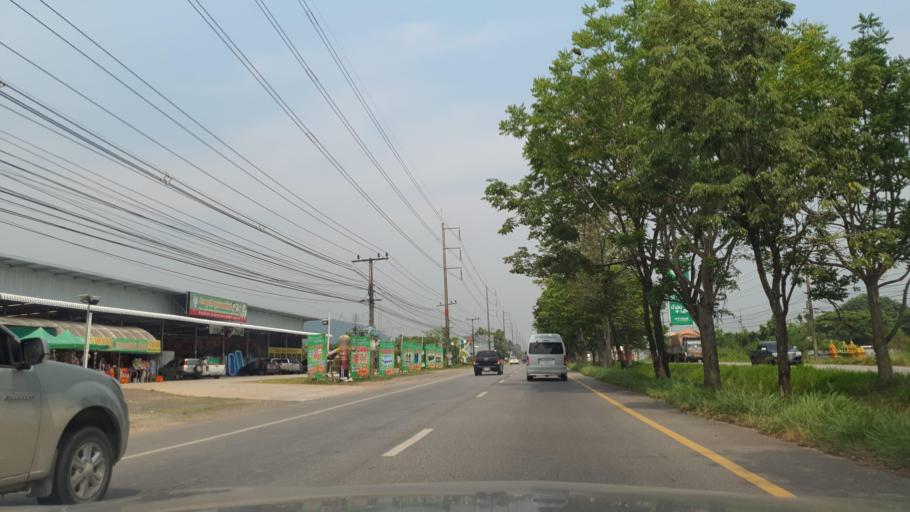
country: TH
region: Rayong
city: Rayong
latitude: 12.6400
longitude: 101.3881
